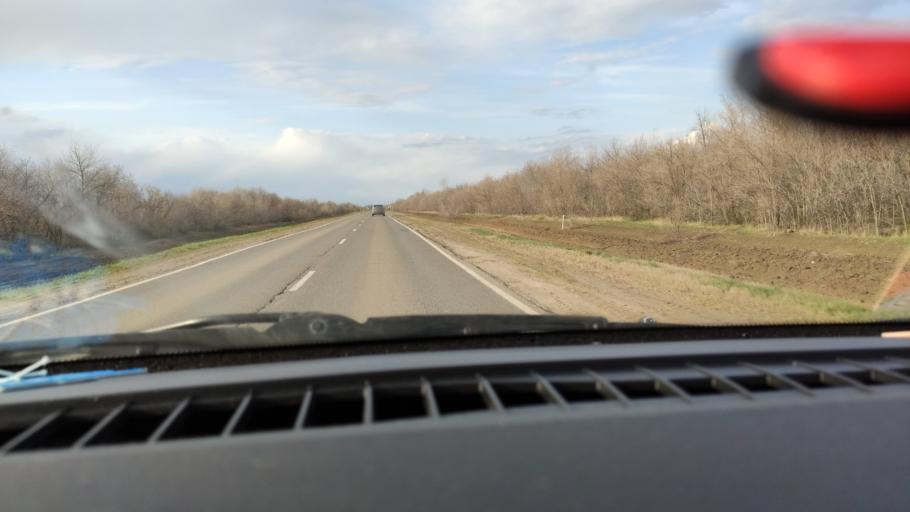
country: RU
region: Saratov
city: Privolzhskiy
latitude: 51.3637
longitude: 46.0453
